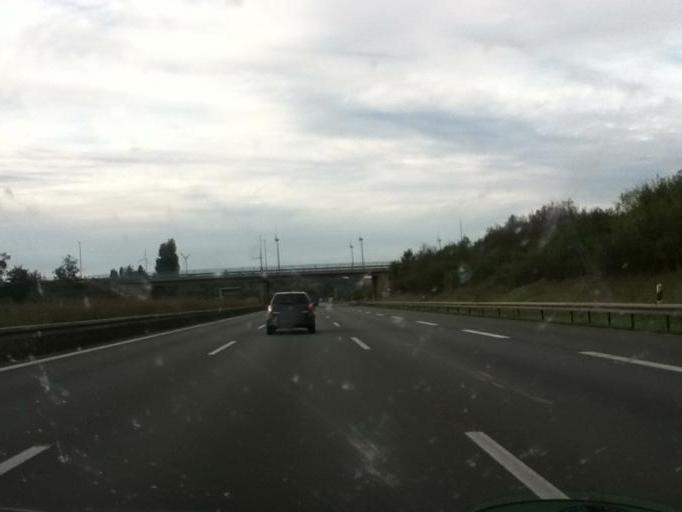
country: DE
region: Saxony
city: Neukirchen
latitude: 50.8270
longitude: 12.8507
